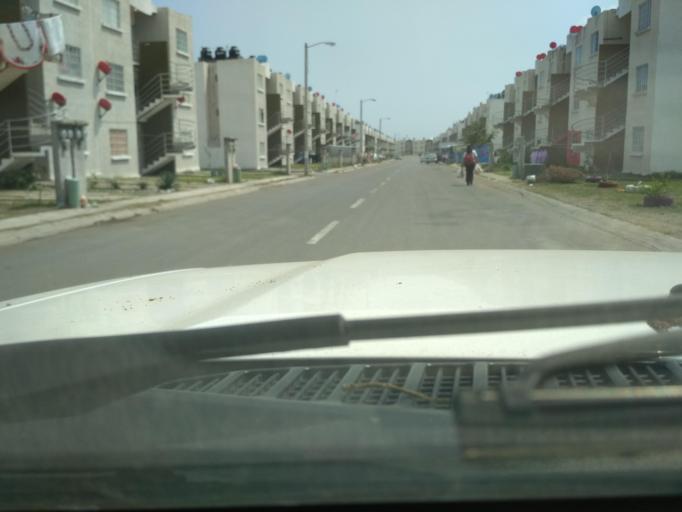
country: MX
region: Veracruz
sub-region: Veracruz
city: Lomas de Rio Medio Cuatro
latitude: 19.1860
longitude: -96.2113
